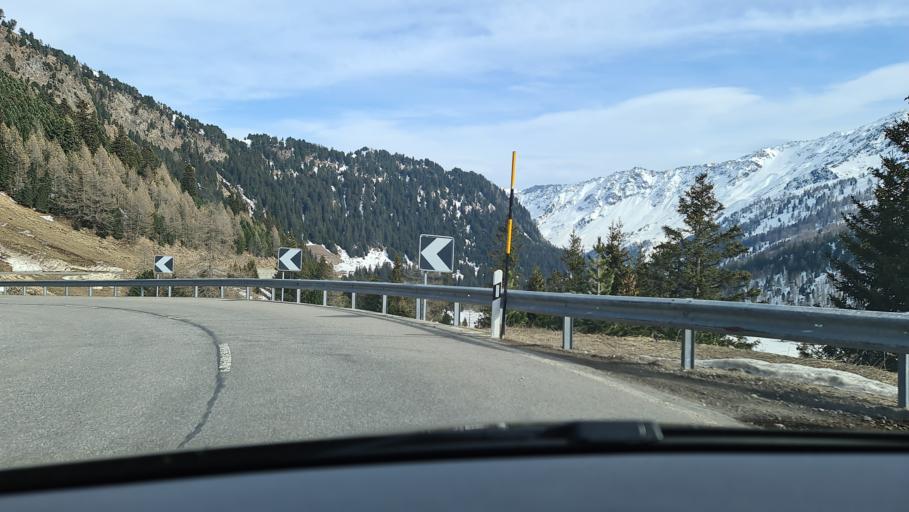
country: CH
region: Ticino
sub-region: Leventina District
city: Faido
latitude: 46.5367
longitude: 8.8359
